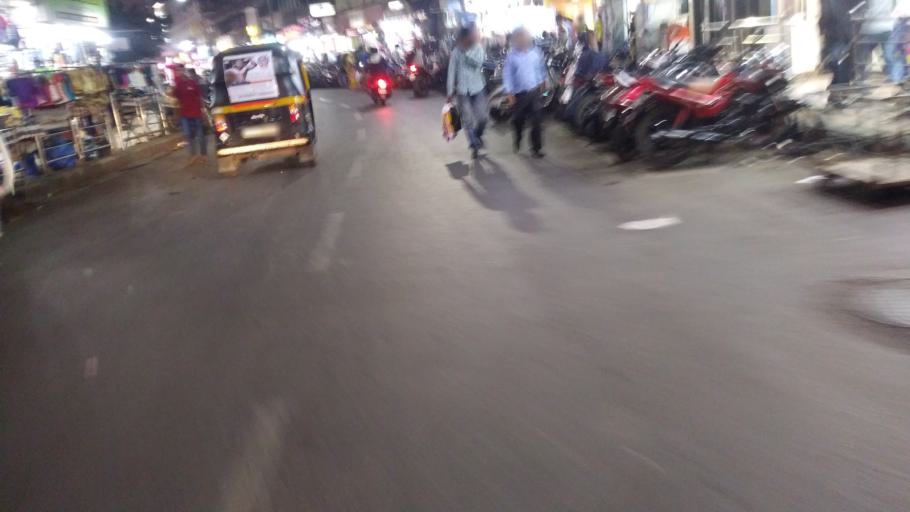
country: IN
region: Maharashtra
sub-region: Pune Division
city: Pune
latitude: 18.5157
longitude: 73.8563
